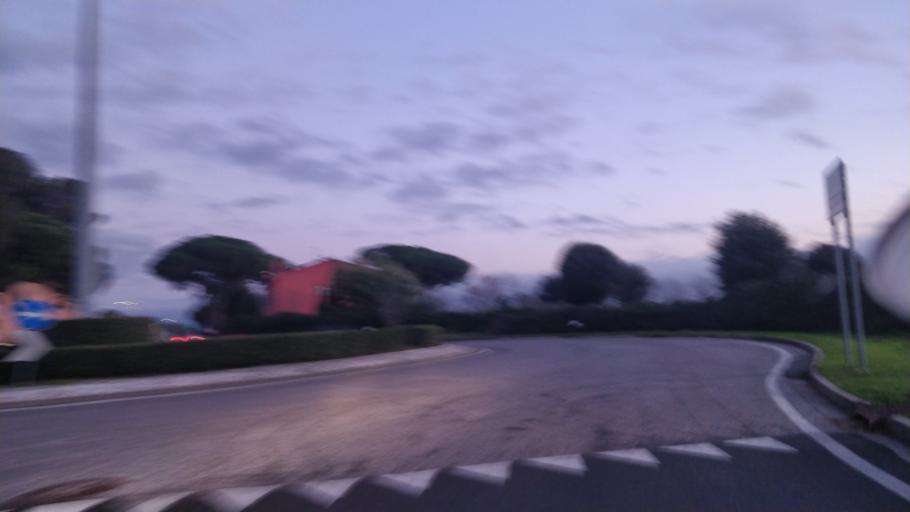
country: IT
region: Tuscany
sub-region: Provincia di Livorno
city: Vada
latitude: 43.3490
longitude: 10.4624
